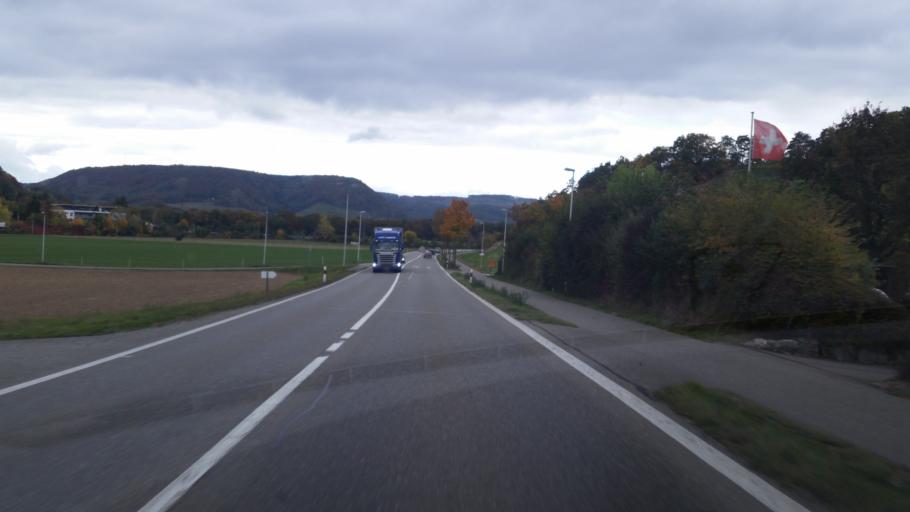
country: CH
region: Aargau
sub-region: Bezirk Brugg
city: Lauffohr (Brugg)
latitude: 47.5047
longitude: 8.2432
